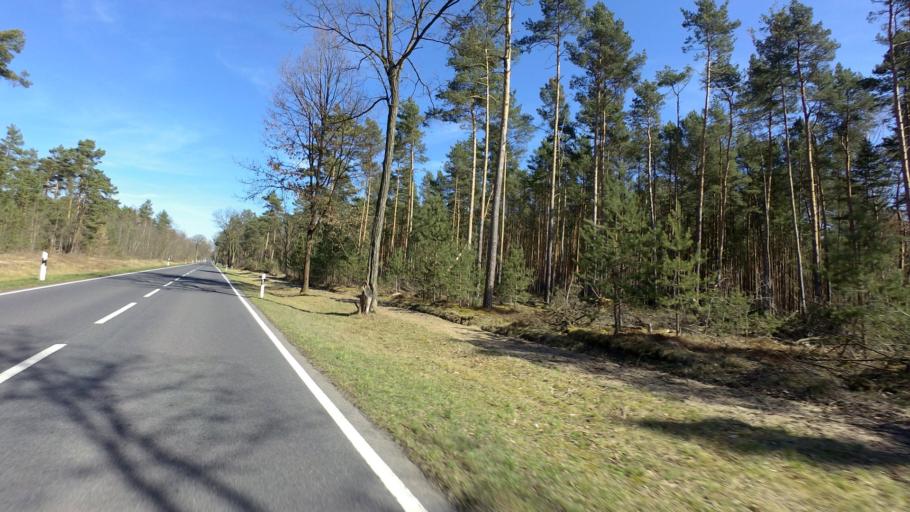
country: DE
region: Brandenburg
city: Storkow
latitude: 52.2048
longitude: 13.9263
